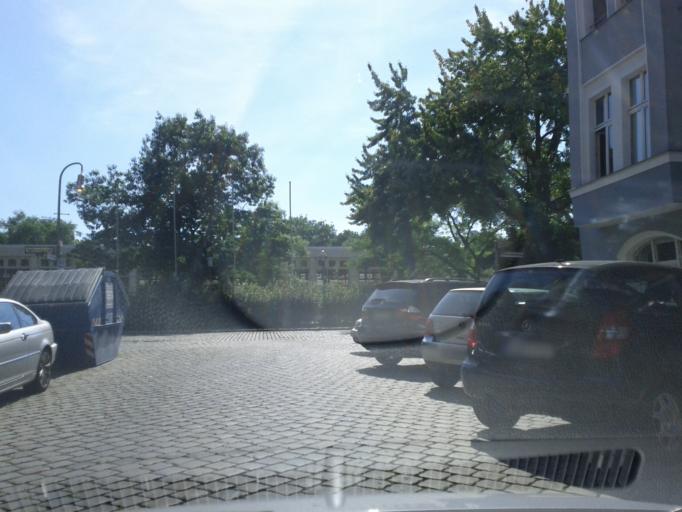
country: DE
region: Berlin
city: Hansaviertel
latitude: 52.5191
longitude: 13.3313
